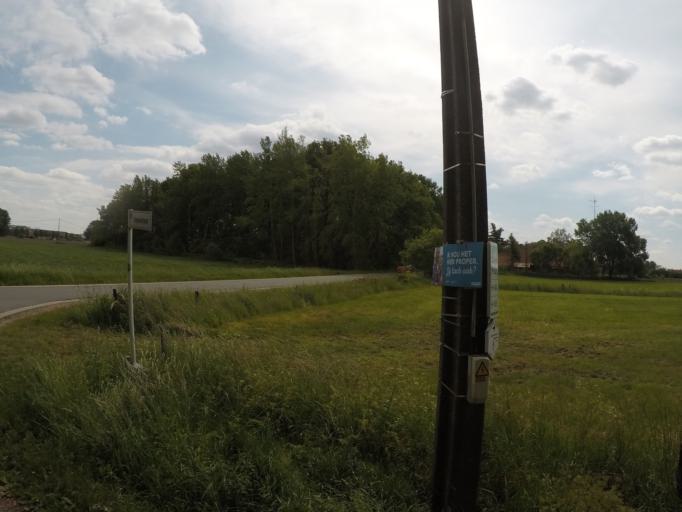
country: BE
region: Flanders
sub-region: Provincie Antwerpen
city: Oostmalle
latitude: 51.3092
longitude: 4.7050
